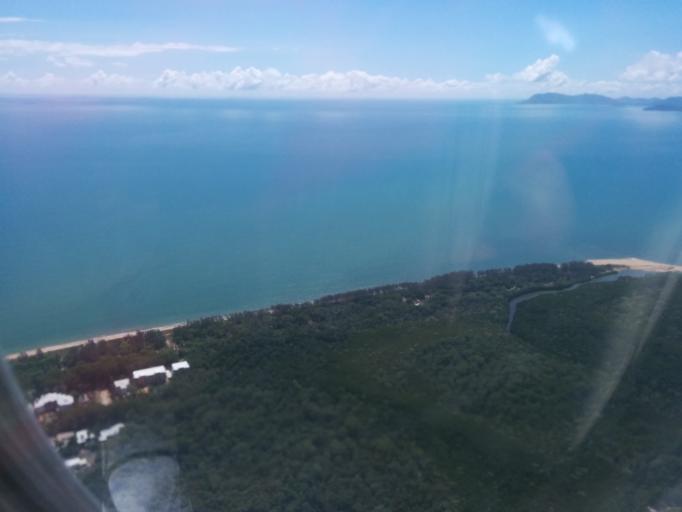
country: AU
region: Queensland
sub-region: Cairns
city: Yorkeys Knob
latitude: -16.8146
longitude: 145.7206
